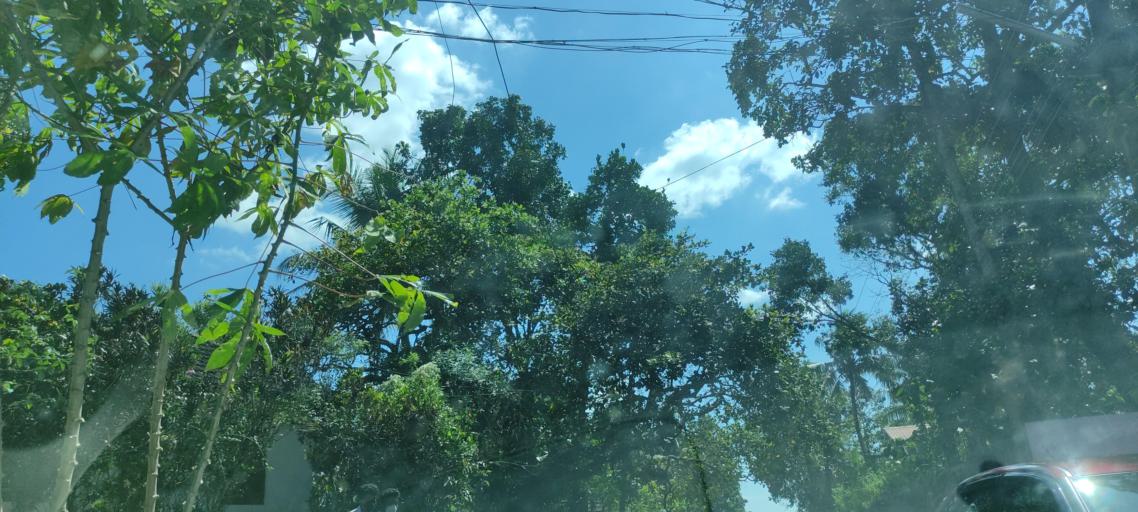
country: IN
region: Kerala
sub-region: Pattanamtitta
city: Adur
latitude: 9.1044
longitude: 76.6884
